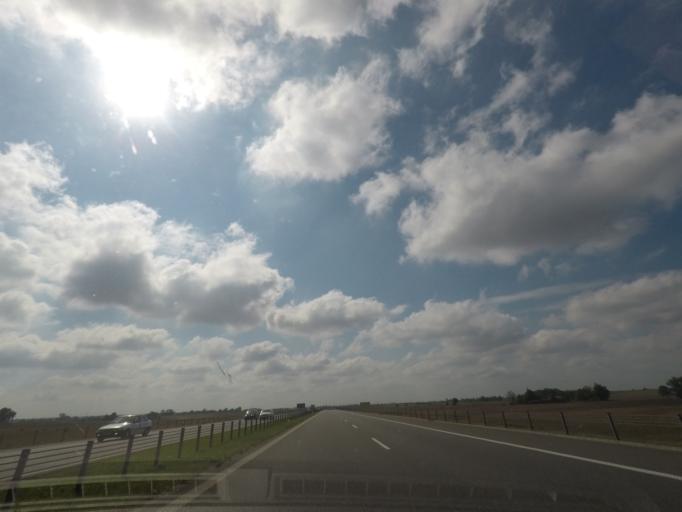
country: PL
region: Kujawsko-Pomorskie
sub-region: Powiat chelminski
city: Lisewo
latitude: 53.2728
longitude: 18.7167
